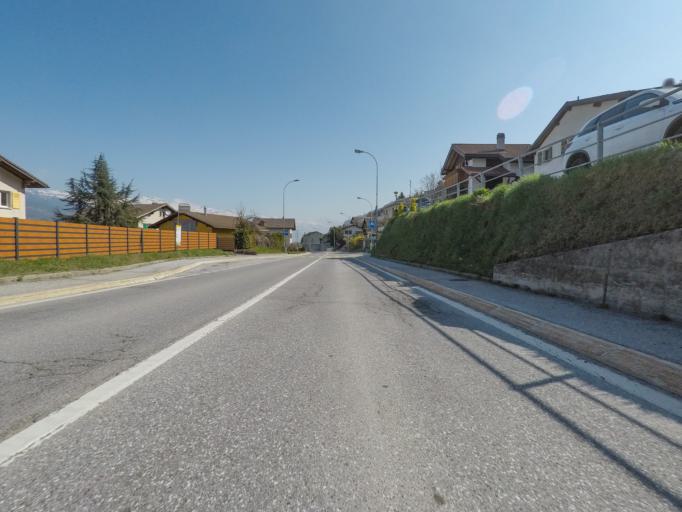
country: CH
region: Valais
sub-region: Sion District
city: Sitten
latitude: 46.2114
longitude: 7.3468
